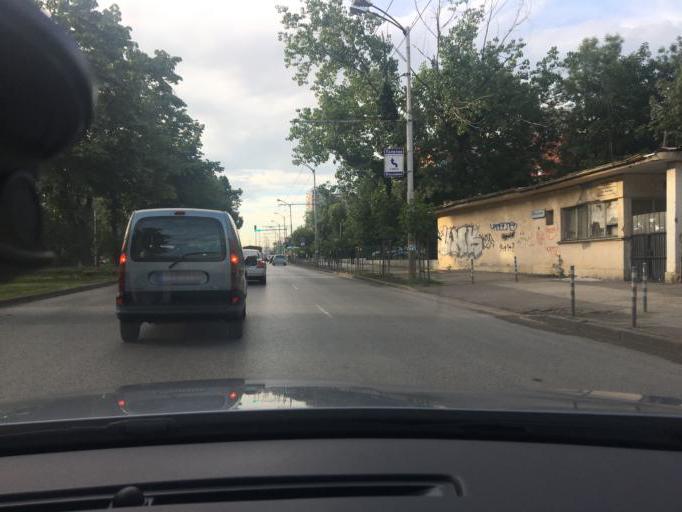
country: BG
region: Sofia-Capital
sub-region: Stolichna Obshtina
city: Sofia
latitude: 42.6811
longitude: 23.3021
